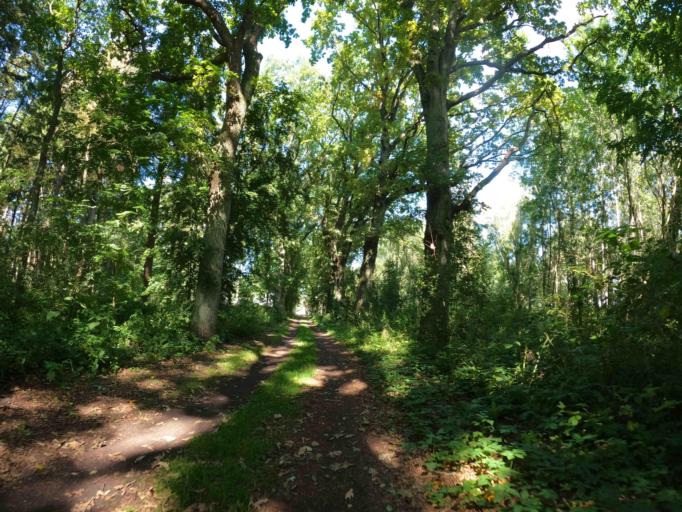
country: DE
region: Mecklenburg-Vorpommern
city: Prohn
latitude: 54.4313
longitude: 13.0313
